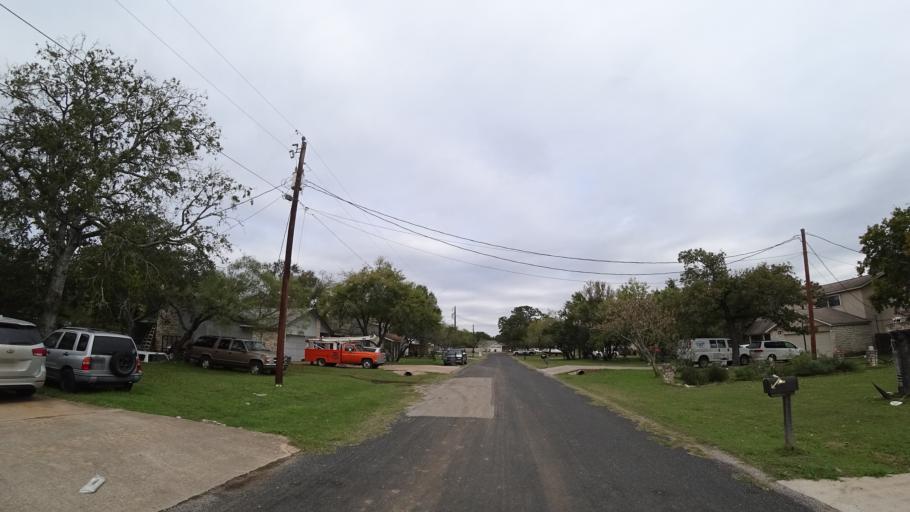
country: US
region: Texas
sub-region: Travis County
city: Shady Hollow
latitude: 30.1457
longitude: -97.8760
